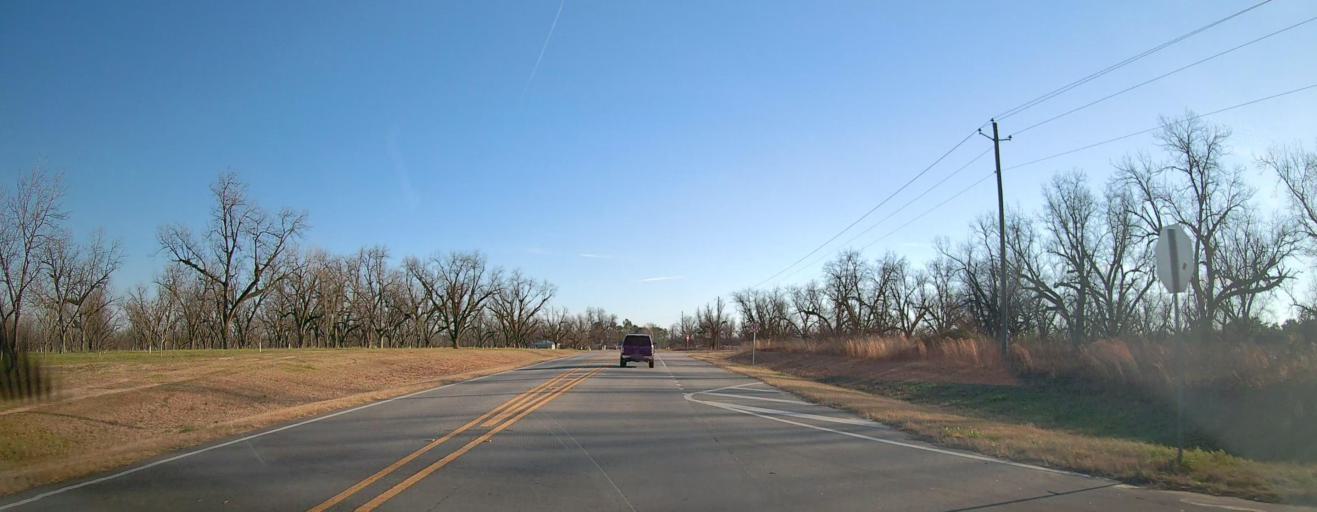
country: US
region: Georgia
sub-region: Dougherty County
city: Albany
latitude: 31.6535
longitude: -84.1710
